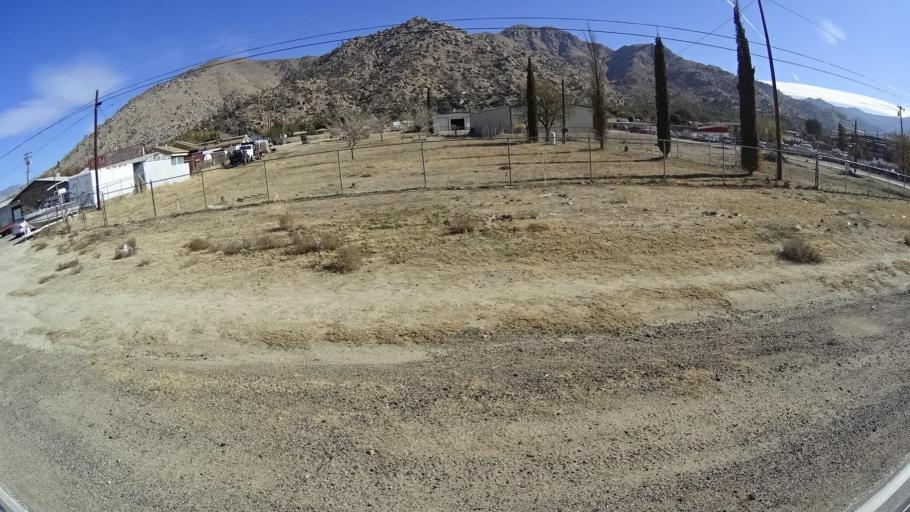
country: US
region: California
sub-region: Kern County
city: Lake Isabella
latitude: 35.6340
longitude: -118.4719
